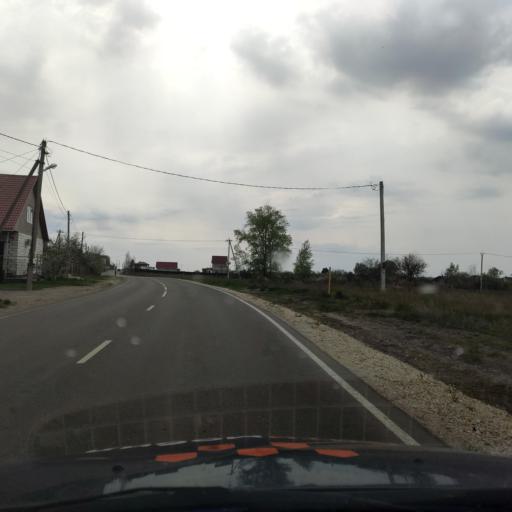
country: RU
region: Voronezj
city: Podgornoye
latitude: 51.8496
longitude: 39.1482
